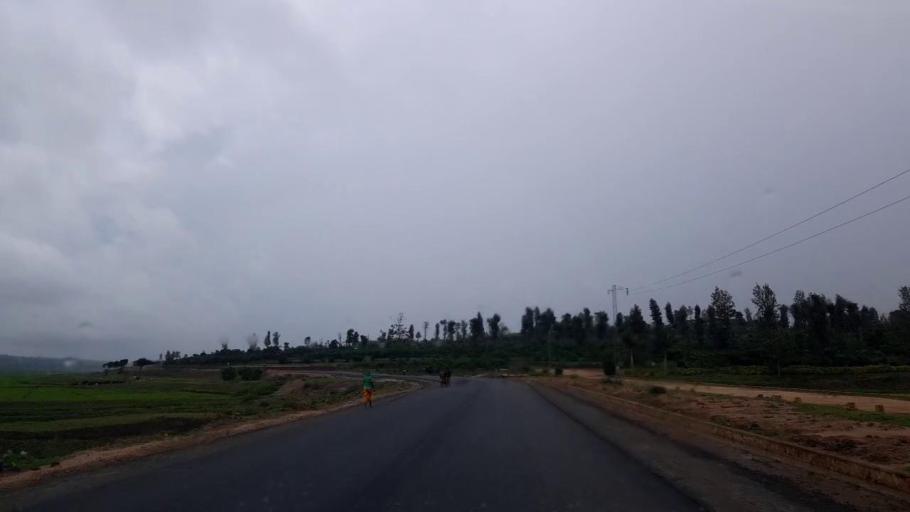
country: RW
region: Northern Province
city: Byumba
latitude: -1.4105
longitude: 30.2849
